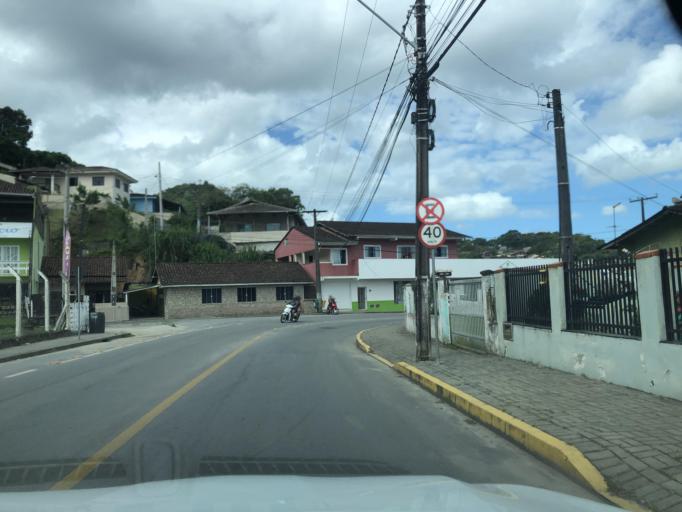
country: BR
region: Santa Catarina
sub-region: Sao Francisco Do Sul
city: Sao Francisco do Sul
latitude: -26.2430
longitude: -48.6297
